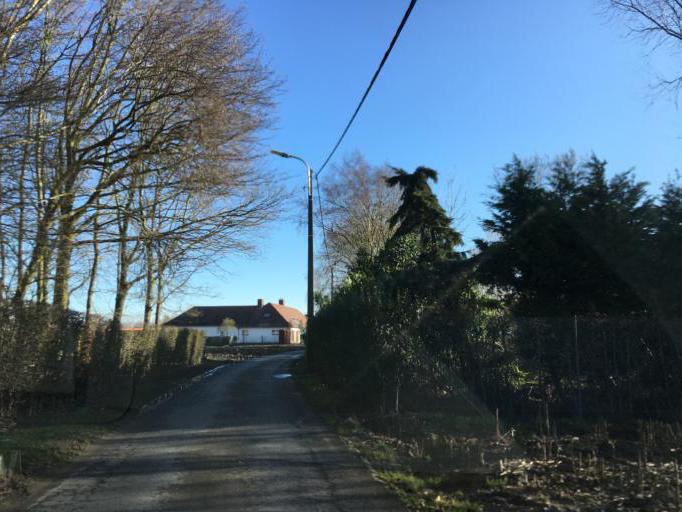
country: BE
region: Flanders
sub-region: Provincie West-Vlaanderen
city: Roeselare
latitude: 50.9177
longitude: 3.1426
